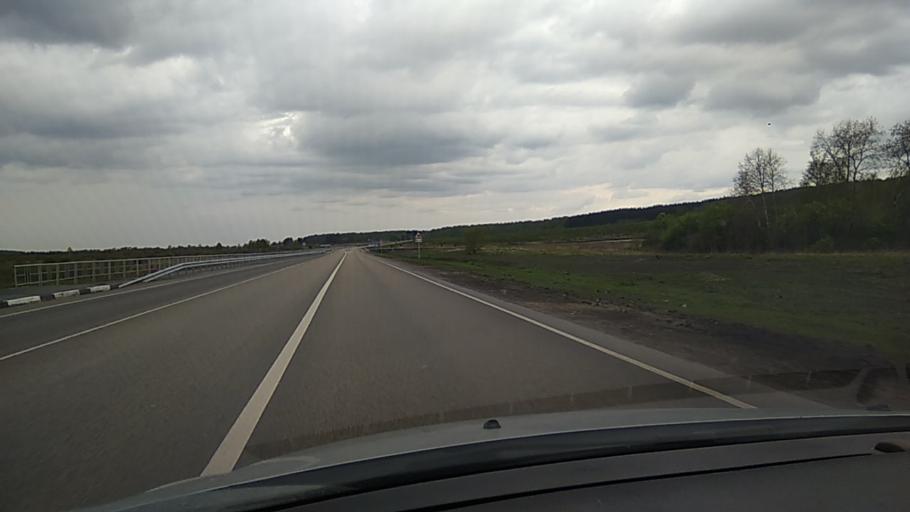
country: RU
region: Kurgan
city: Kataysk
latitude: 56.2972
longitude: 62.4157
